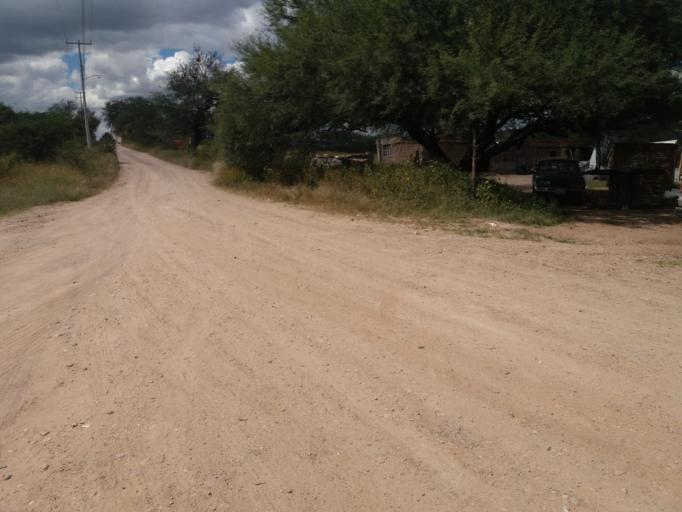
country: MX
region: Aguascalientes
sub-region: Aguascalientes
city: San Sebastian [Fraccionamiento]
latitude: 21.8058
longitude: -102.2435
